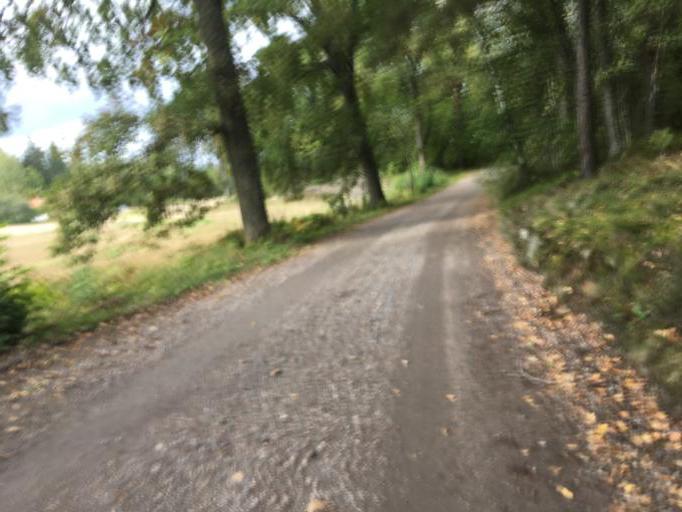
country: SE
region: Soedermanland
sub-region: Eskilstuna Kommun
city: Arla
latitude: 59.4598
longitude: 16.6778
